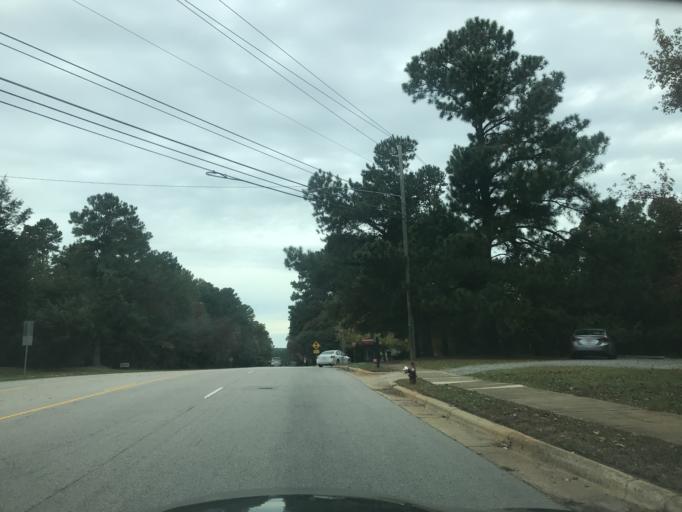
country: US
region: North Carolina
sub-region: Wake County
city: West Raleigh
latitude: 35.8563
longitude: -78.6468
